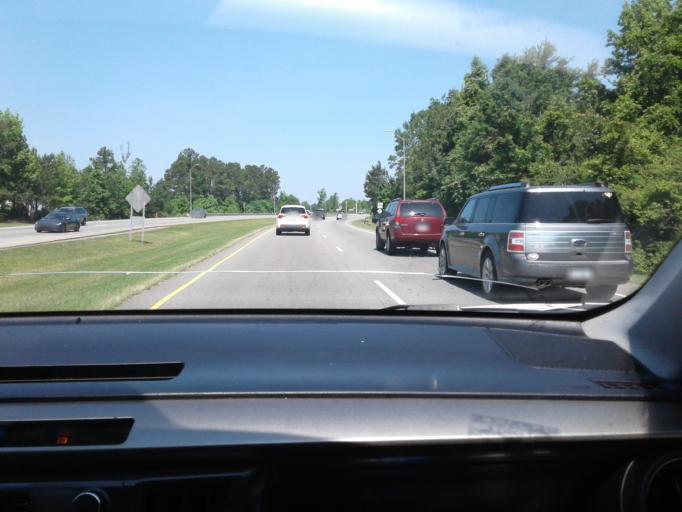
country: US
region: North Carolina
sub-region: Wake County
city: Holly Springs
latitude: 35.6400
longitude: -78.8344
